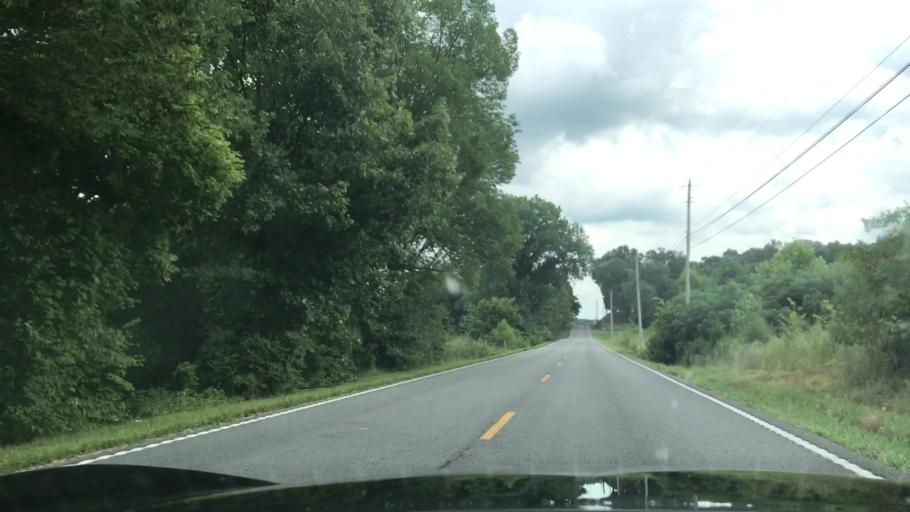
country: US
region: Kentucky
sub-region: Muhlenberg County
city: Greenville
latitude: 37.1976
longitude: -87.1222
